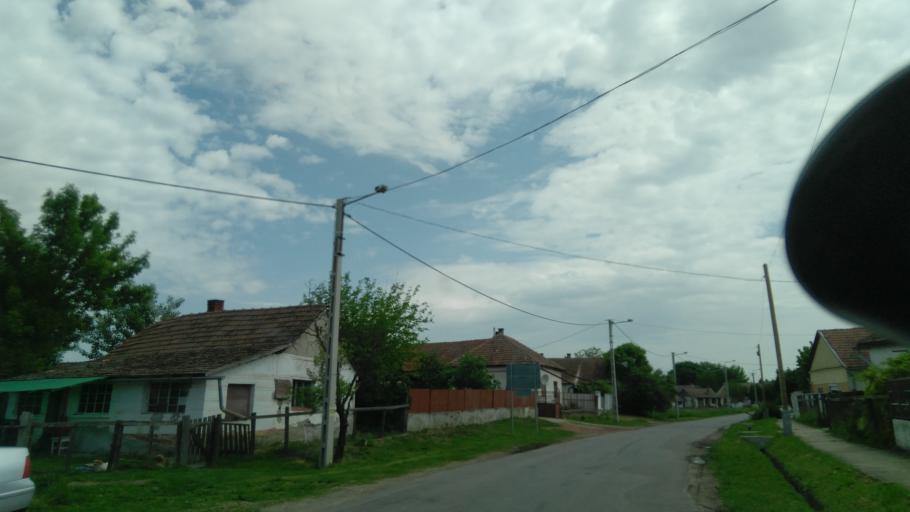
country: HU
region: Hajdu-Bihar
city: Komadi
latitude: 47.0184
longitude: 21.5966
